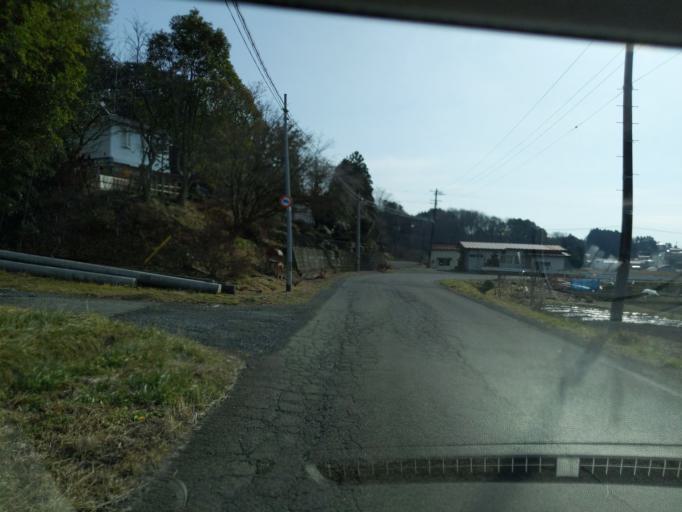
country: JP
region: Miyagi
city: Wakuya
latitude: 38.7062
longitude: 141.1575
